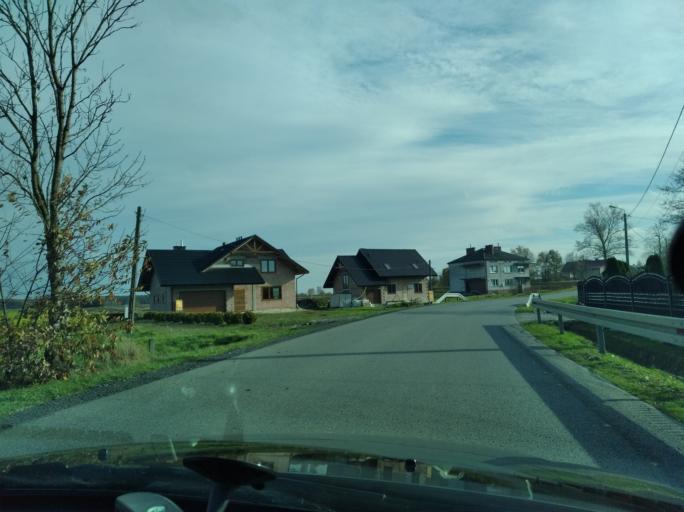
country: PL
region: Subcarpathian Voivodeship
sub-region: Powiat ropczycko-sedziszowski
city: Sedziszow Malopolski
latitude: 50.0898
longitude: 21.7460
